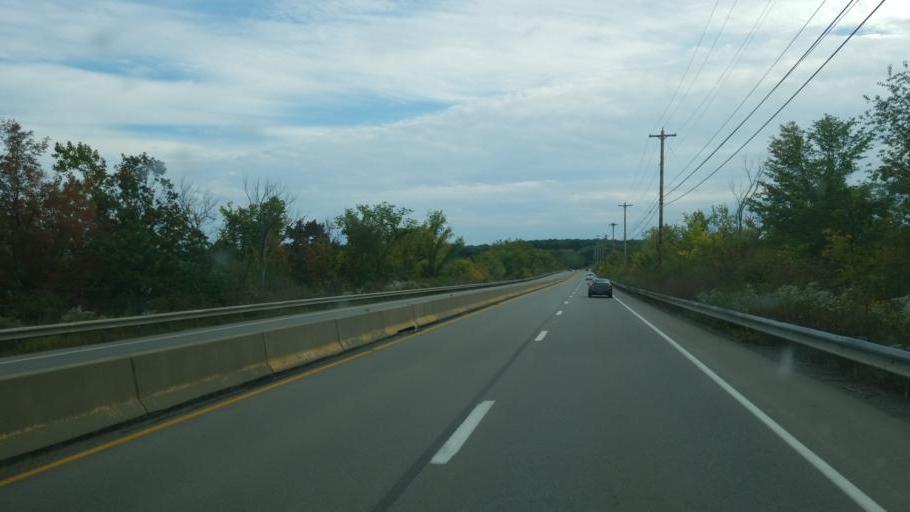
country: US
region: Pennsylvania
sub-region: Mercer County
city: Sharpsville
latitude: 41.2912
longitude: -80.4272
